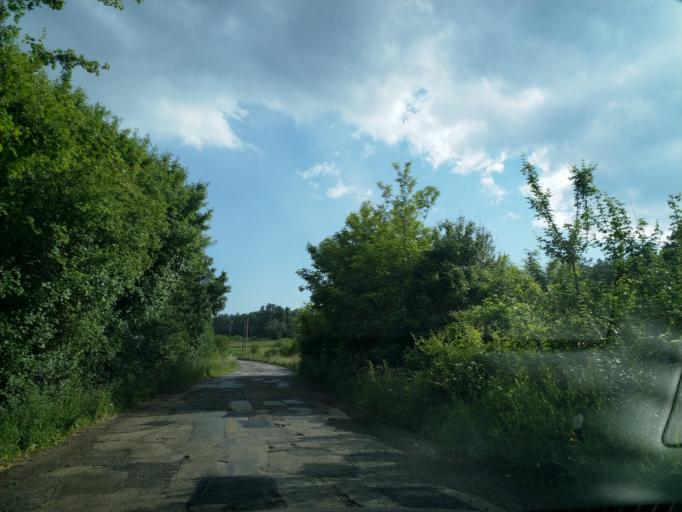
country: RS
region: Central Serbia
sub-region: Zajecarski Okrug
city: Boljevac
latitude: 43.9768
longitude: 21.9729
